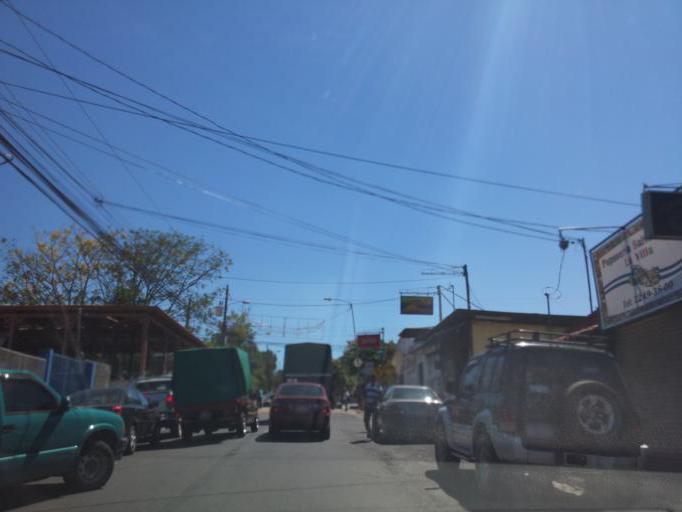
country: CR
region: Heredia
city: Colon
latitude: 9.9153
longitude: -84.2418
